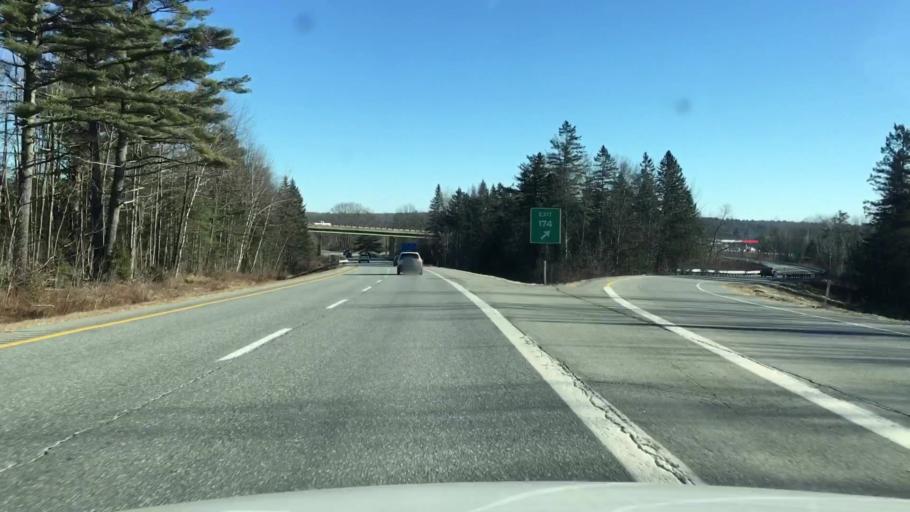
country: US
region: Maine
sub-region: Penobscot County
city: Hermon
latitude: 44.7588
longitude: -68.9777
